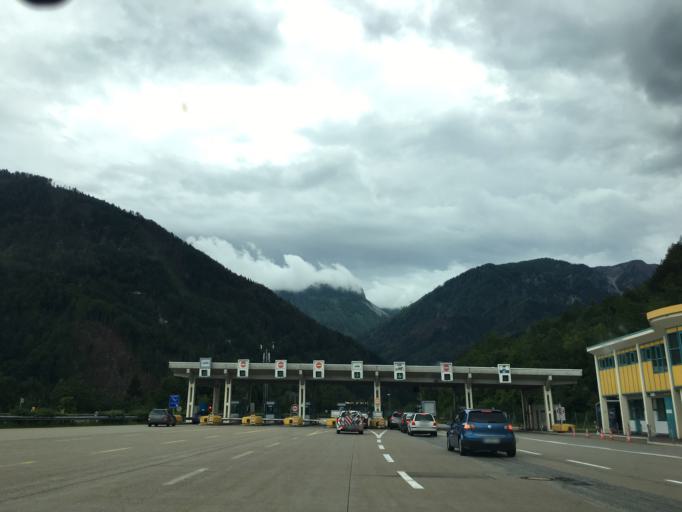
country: AT
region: Carinthia
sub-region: Politischer Bezirk Villach Land
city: Sankt Jakob
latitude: 46.5278
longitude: 14.0307
